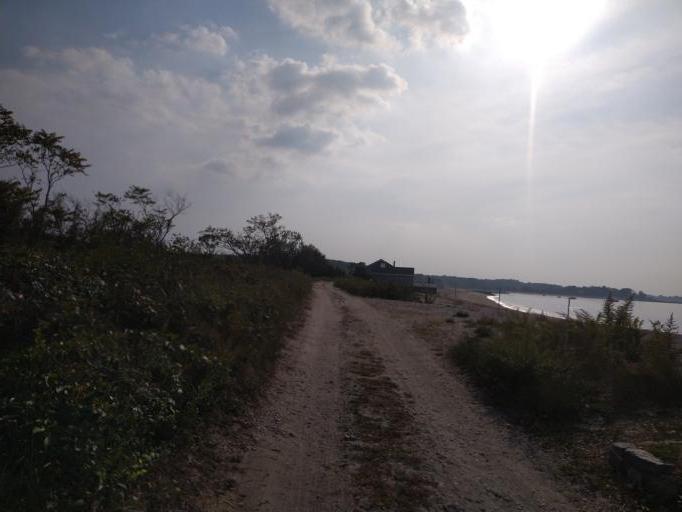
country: US
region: New York
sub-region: Nassau County
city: Lattingtown
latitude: 40.9064
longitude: -73.5955
